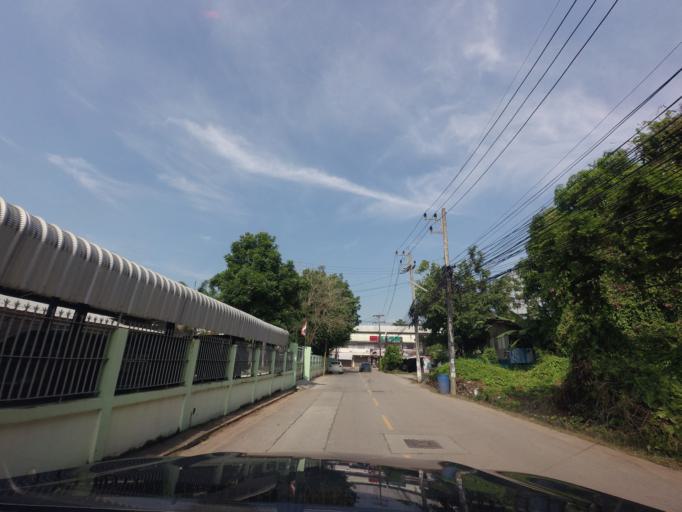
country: TH
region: Khon Kaen
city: Khon Kaen
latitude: 16.4189
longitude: 102.8243
